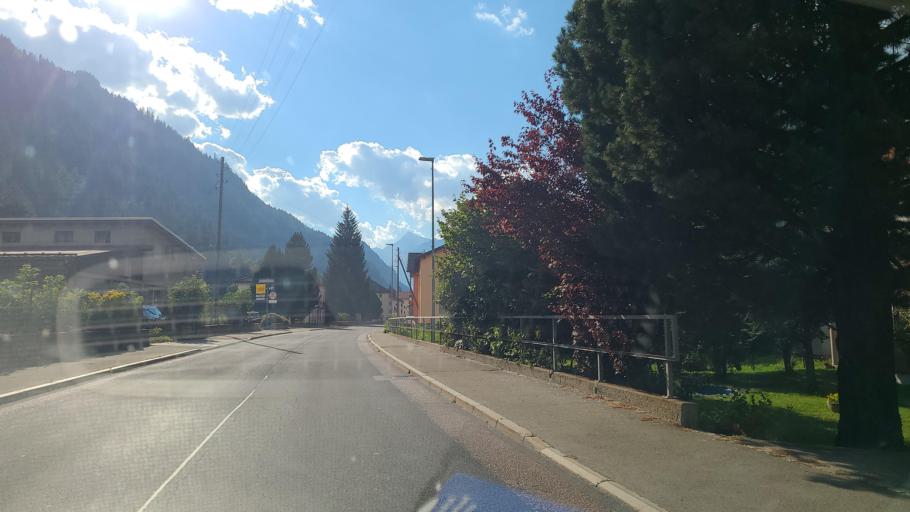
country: CH
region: Ticino
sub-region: Leventina District
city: Airolo
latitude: 46.5083
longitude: 8.7001
